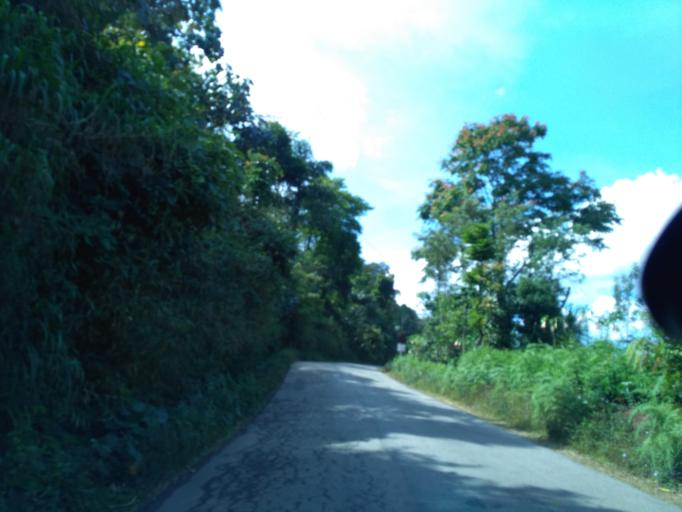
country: IN
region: Karnataka
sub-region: Kodagu
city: Madikeri
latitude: 12.3553
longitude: 75.6489
